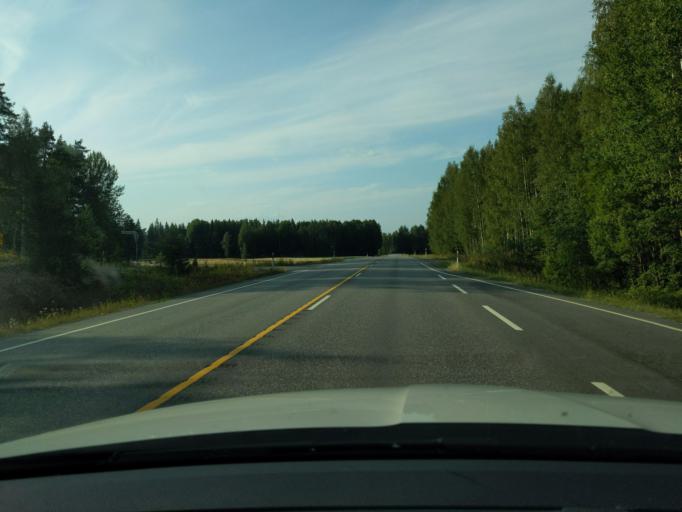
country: FI
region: Paijanne Tavastia
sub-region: Lahti
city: Padasjoki
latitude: 61.3103
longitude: 25.2921
